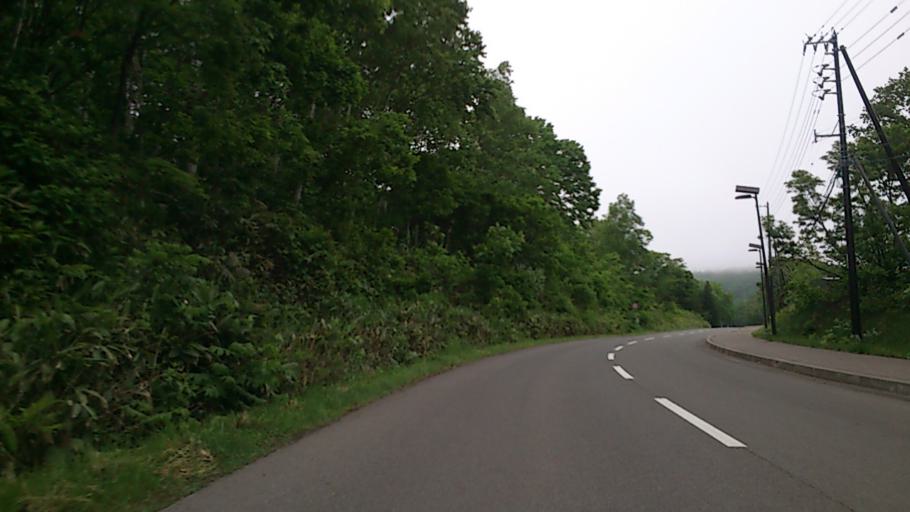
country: JP
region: Hokkaido
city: Niseko Town
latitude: 42.8431
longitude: 140.6392
